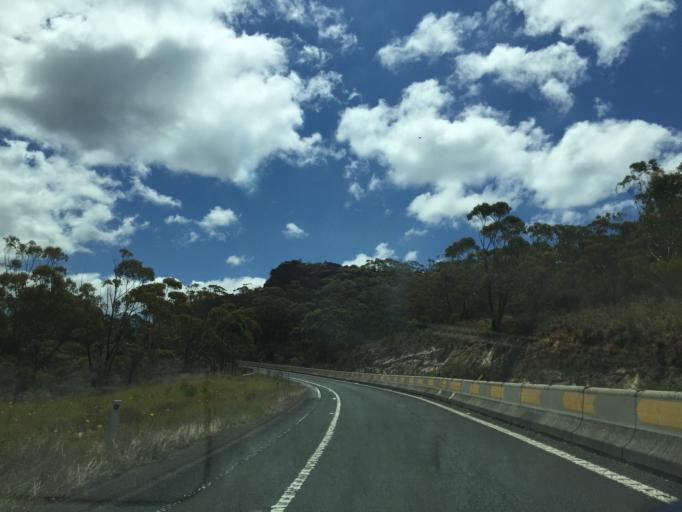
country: AU
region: New South Wales
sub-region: Blue Mountains Municipality
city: Blackheath
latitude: -33.5262
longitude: 150.3101
